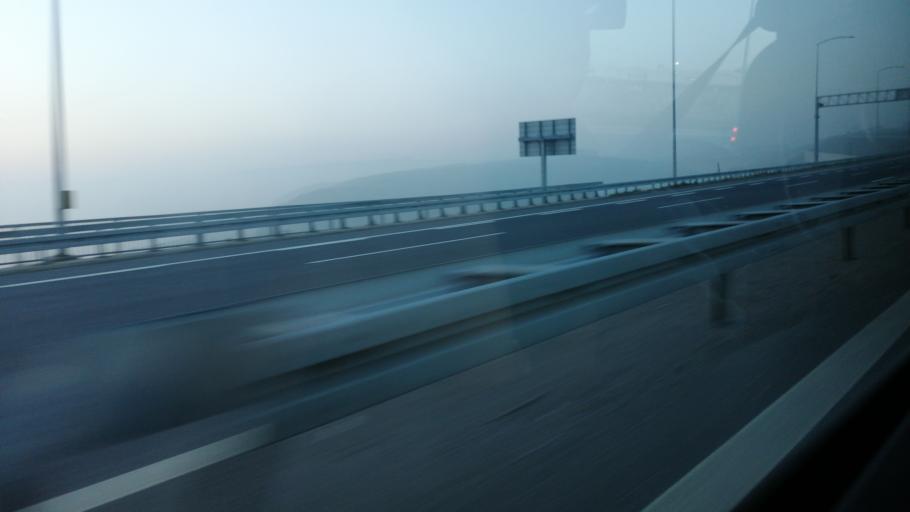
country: TR
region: Kocaeli
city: Tavsanli
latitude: 40.7703
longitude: 29.5183
